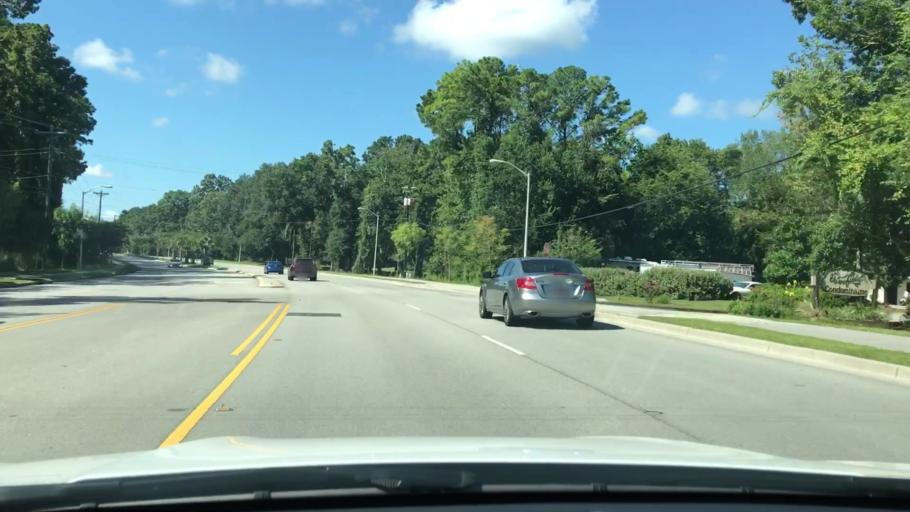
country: US
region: South Carolina
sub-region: Charleston County
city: Shell Point
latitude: 32.8403
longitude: -80.0635
